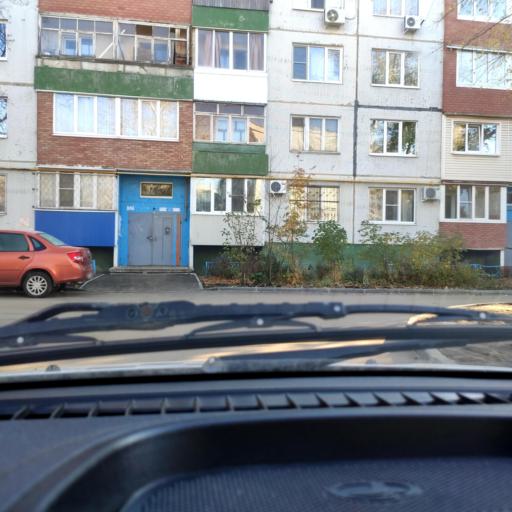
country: RU
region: Samara
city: Zhigulevsk
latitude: 53.4852
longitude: 49.4848
